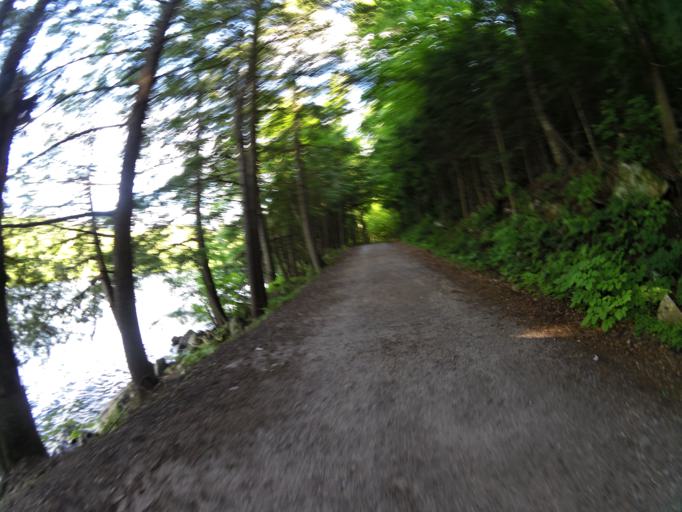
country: CA
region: Quebec
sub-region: Outaouais
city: Wakefield
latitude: 45.5902
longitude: -75.9839
